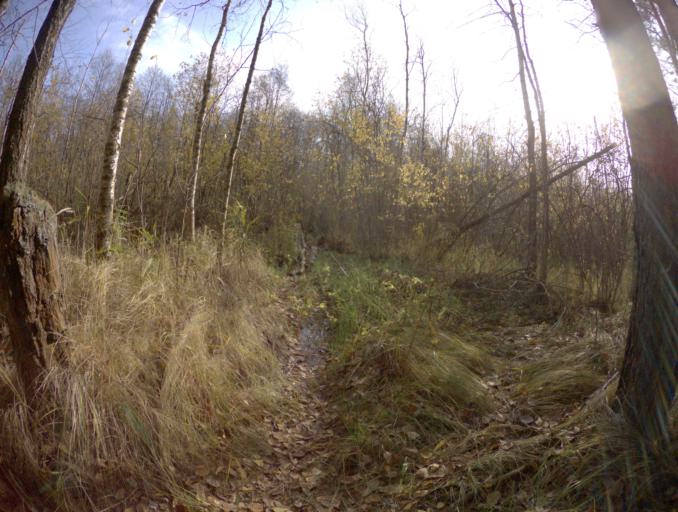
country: RU
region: Vladimir
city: Kommunar
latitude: 56.1161
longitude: 40.4687
